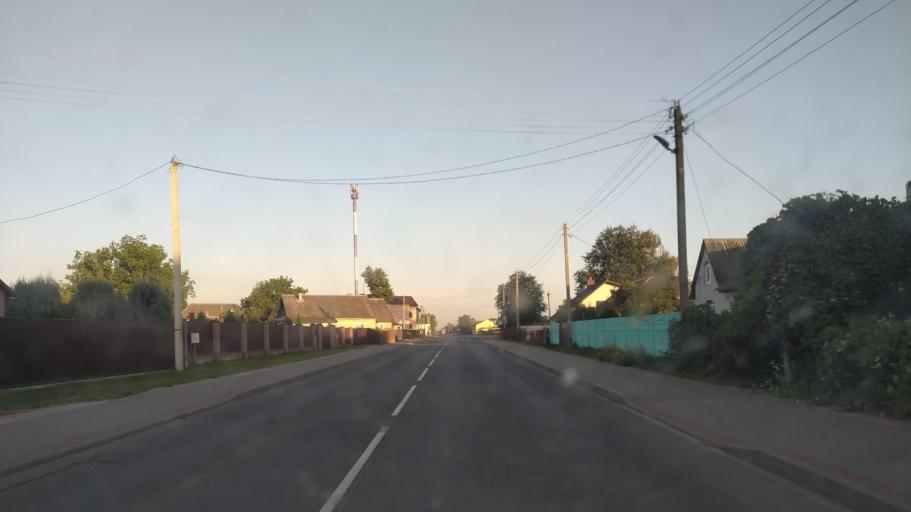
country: BY
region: Brest
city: Byaroza
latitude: 52.5397
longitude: 24.9809
